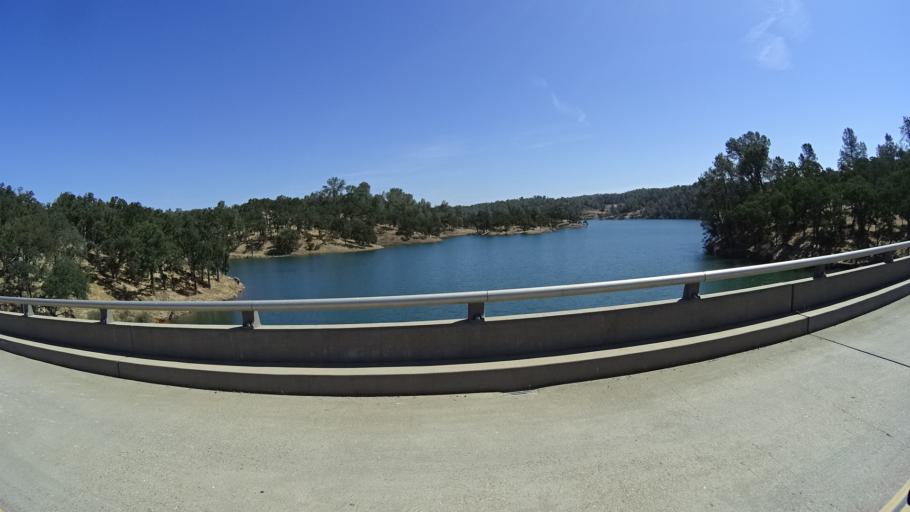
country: US
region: California
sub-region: Calaveras County
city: Valley Springs
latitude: 38.2271
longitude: -120.8890
